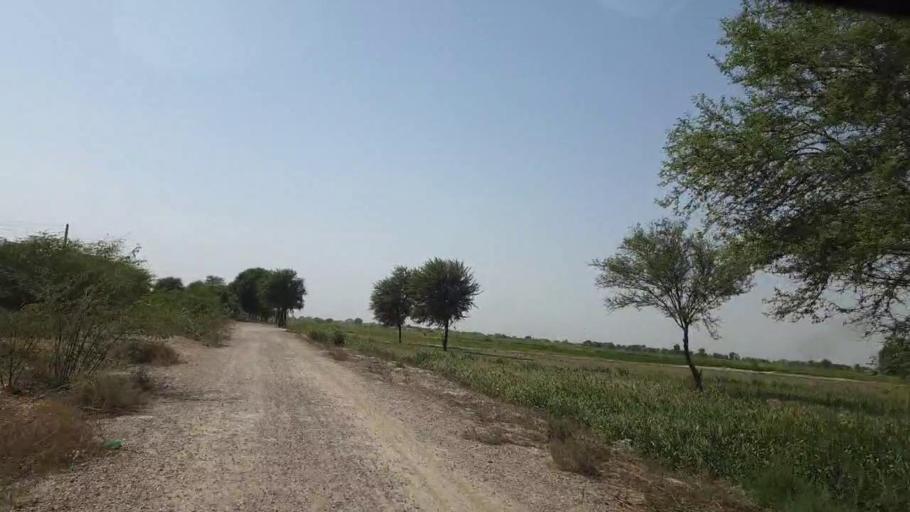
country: PK
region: Sindh
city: Nabisar
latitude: 25.0829
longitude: 69.5647
